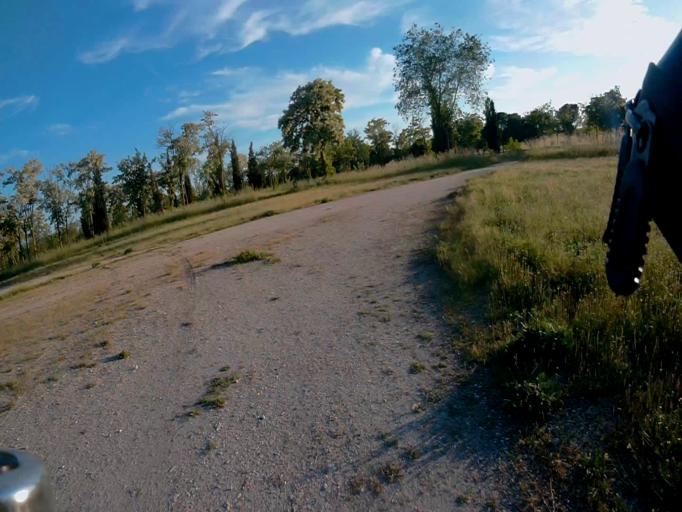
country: ES
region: Madrid
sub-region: Provincia de Madrid
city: Alcorcon
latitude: 40.3200
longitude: -3.8005
